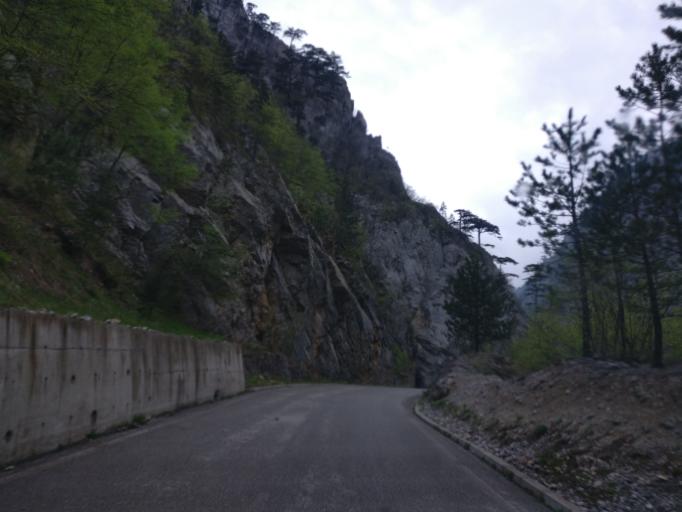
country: ME
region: Opstina Pluzine
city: Pluzine
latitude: 43.2801
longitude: 18.8493
